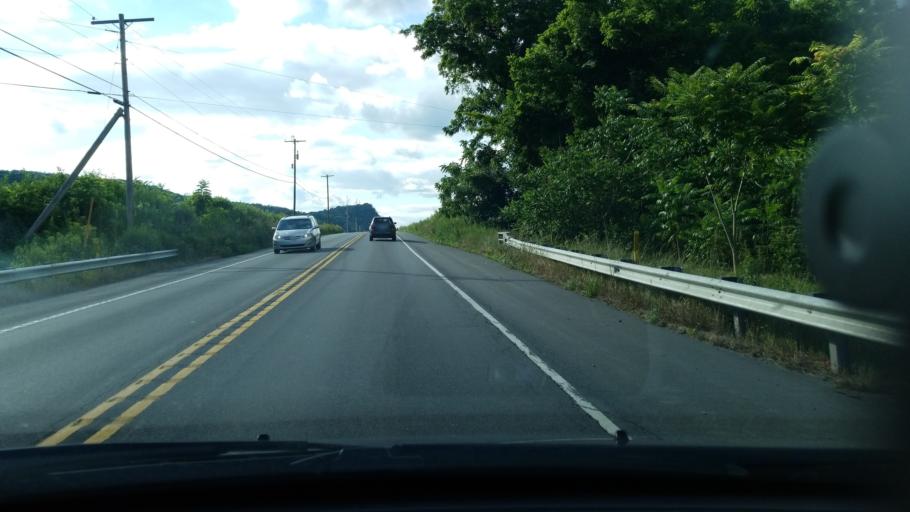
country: US
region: Pennsylvania
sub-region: Montour County
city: Mechanicsville
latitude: 40.9331
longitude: -76.5951
